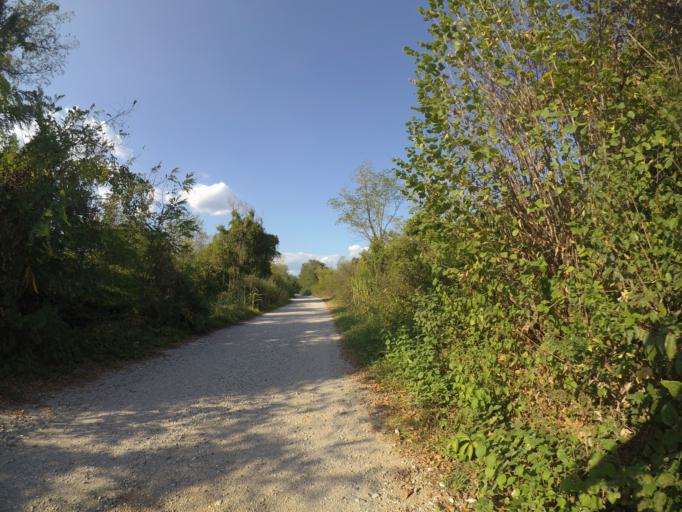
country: IT
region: Friuli Venezia Giulia
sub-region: Provincia di Udine
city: Basaldella
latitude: 46.0237
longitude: 13.1980
